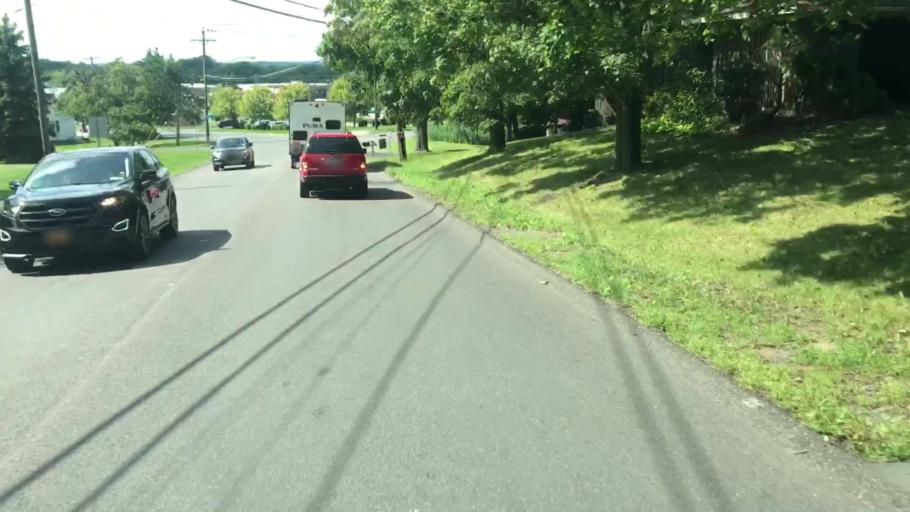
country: US
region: New York
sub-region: Cayuga County
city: Auburn
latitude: 42.9523
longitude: -76.5418
